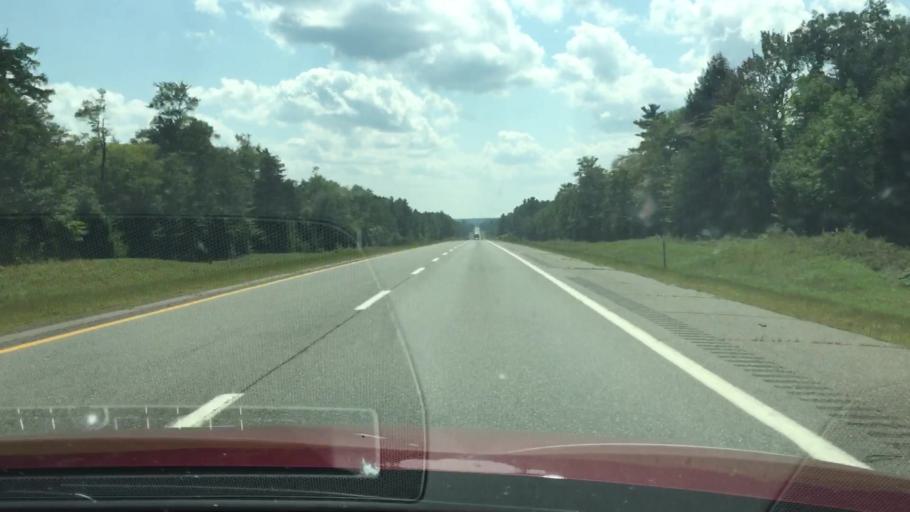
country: US
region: Maine
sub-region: Penobscot County
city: Lincoln
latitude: 45.4175
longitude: -68.5926
